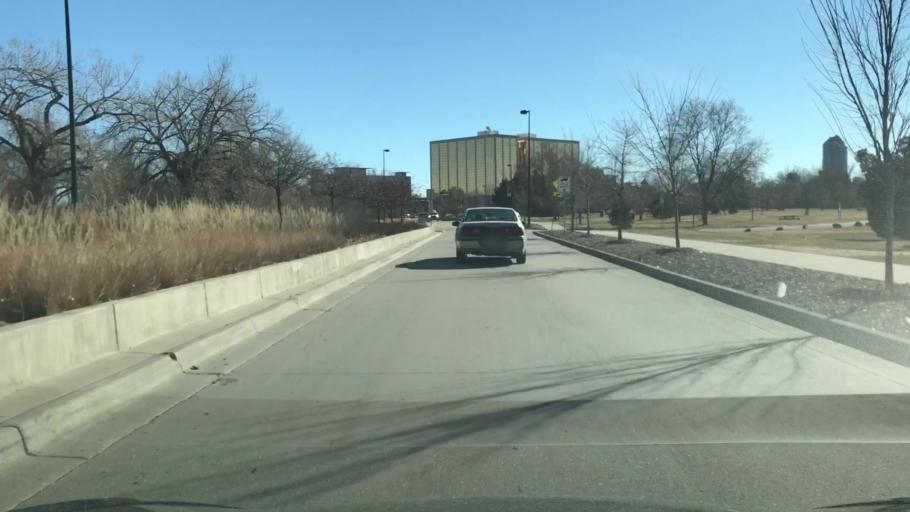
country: US
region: Colorado
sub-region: Arapahoe County
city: Glendale
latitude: 39.7086
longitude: -104.9451
